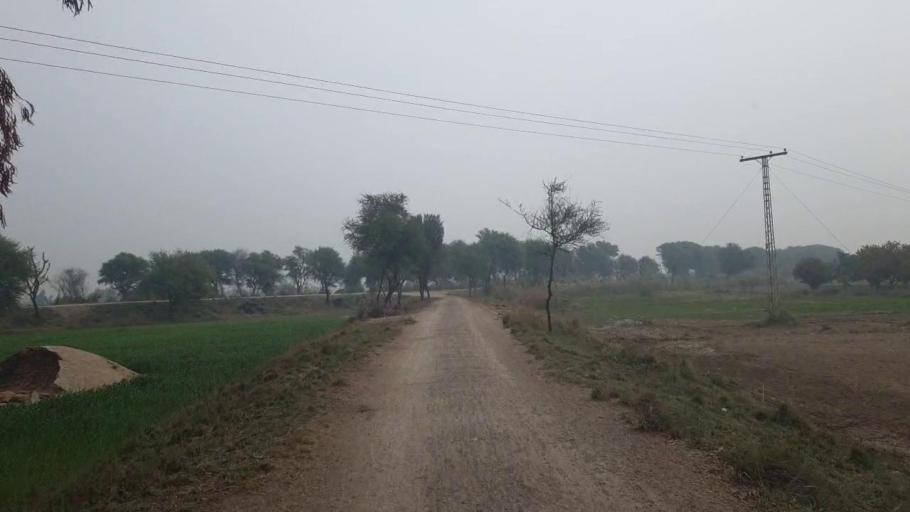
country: PK
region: Sindh
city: Tando Adam
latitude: 25.7523
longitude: 68.6985
